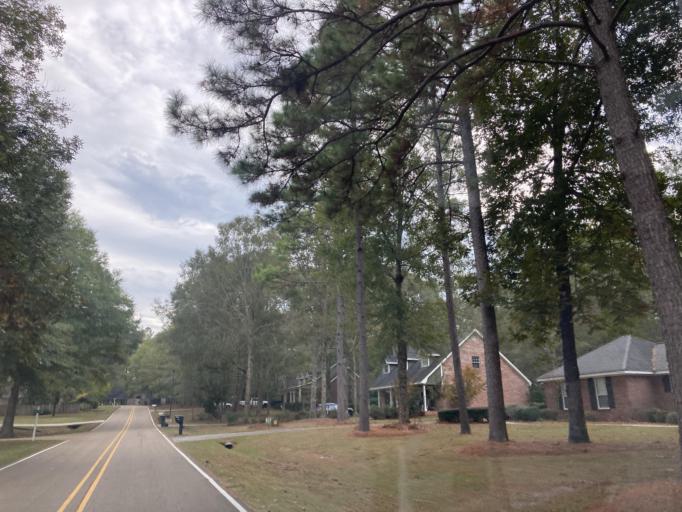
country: US
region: Mississippi
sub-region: Lamar County
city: West Hattiesburg
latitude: 31.3089
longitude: -89.4673
